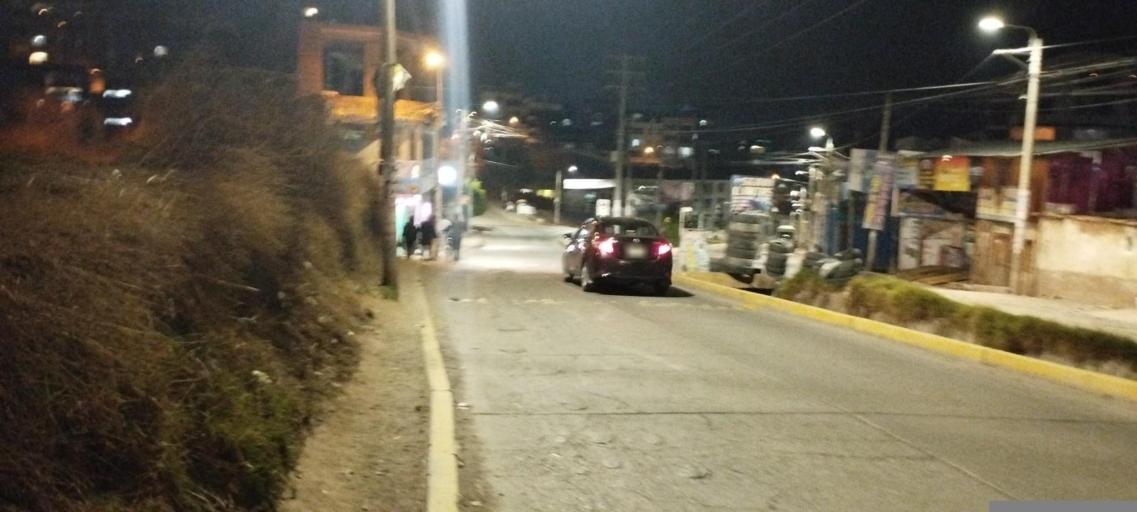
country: PE
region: Cusco
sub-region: Provincia de Cusco
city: Cusco
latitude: -13.5228
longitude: -71.9451
